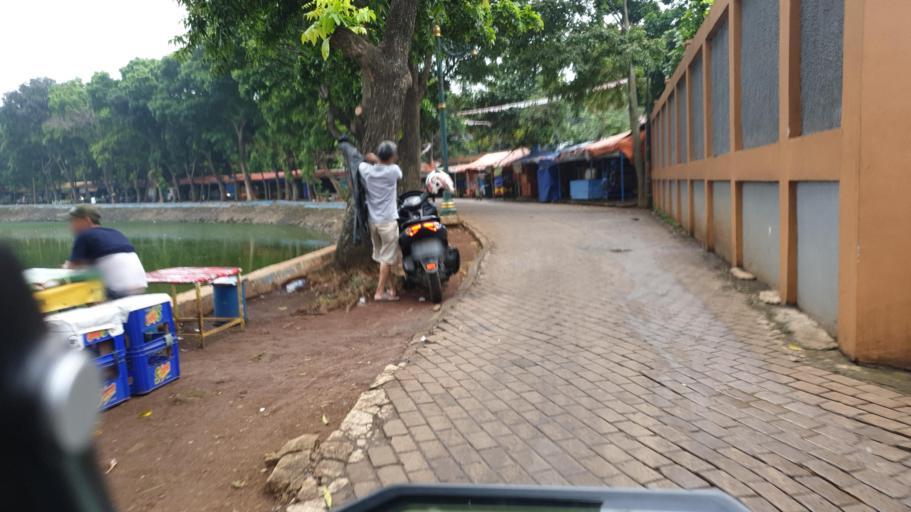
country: ID
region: West Java
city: Depok
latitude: -6.3406
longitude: 106.8264
